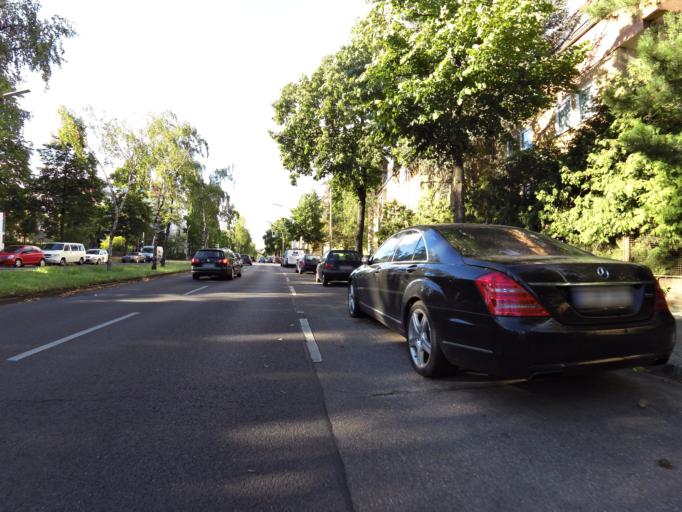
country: DE
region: Berlin
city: Steglitz Bezirk
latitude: 52.4552
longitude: 13.3326
